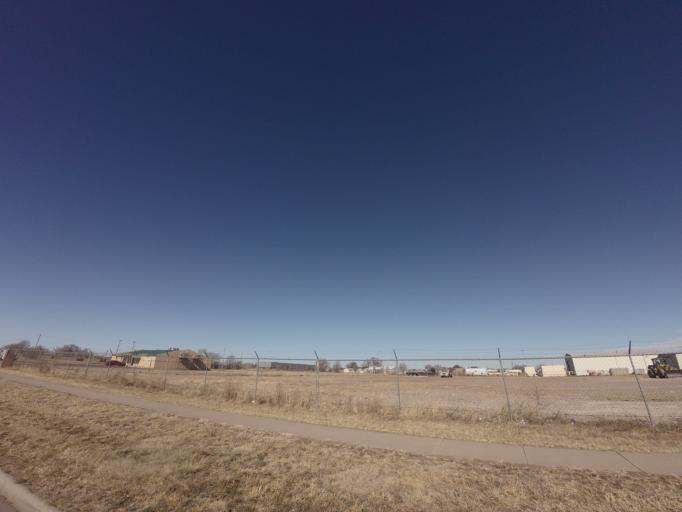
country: US
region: New Mexico
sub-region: Curry County
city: Clovis
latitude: 34.4008
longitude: -103.2375
